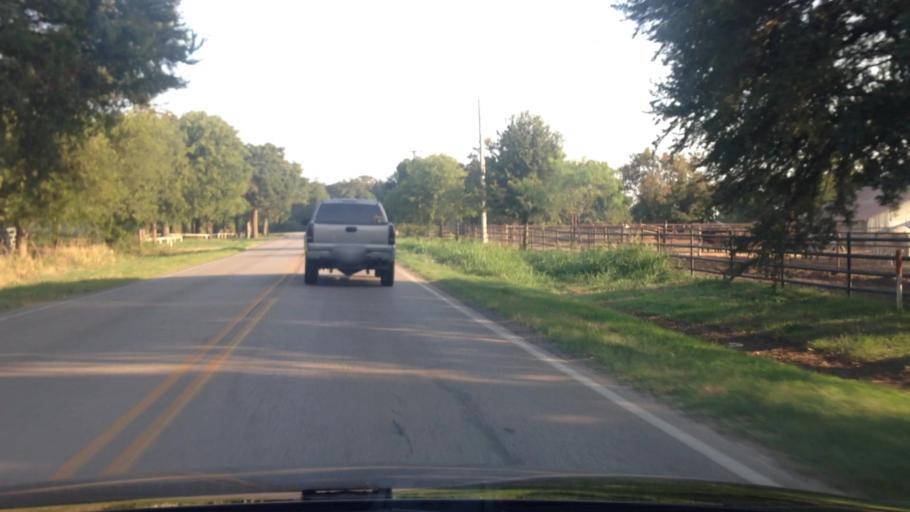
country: US
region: Texas
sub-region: Tarrant County
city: Everman
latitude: 32.6082
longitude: -97.2673
